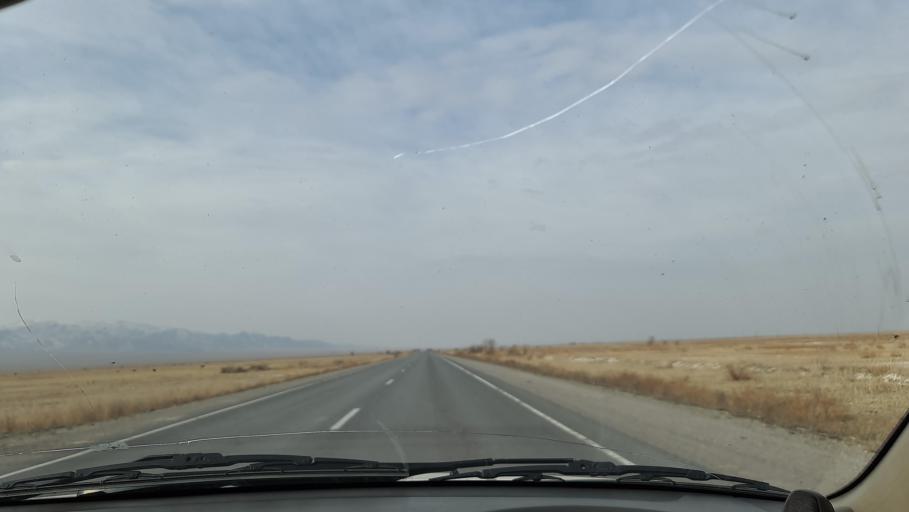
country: KG
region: Chuy
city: Tokmok
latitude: 43.3536
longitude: 75.4469
